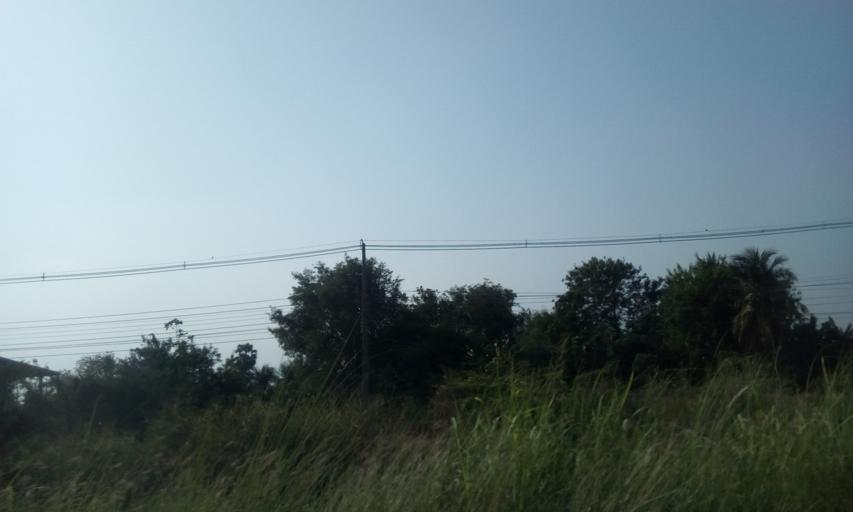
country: TH
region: Sing Buri
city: Phrom Buri
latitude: 14.8320
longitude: 100.4328
